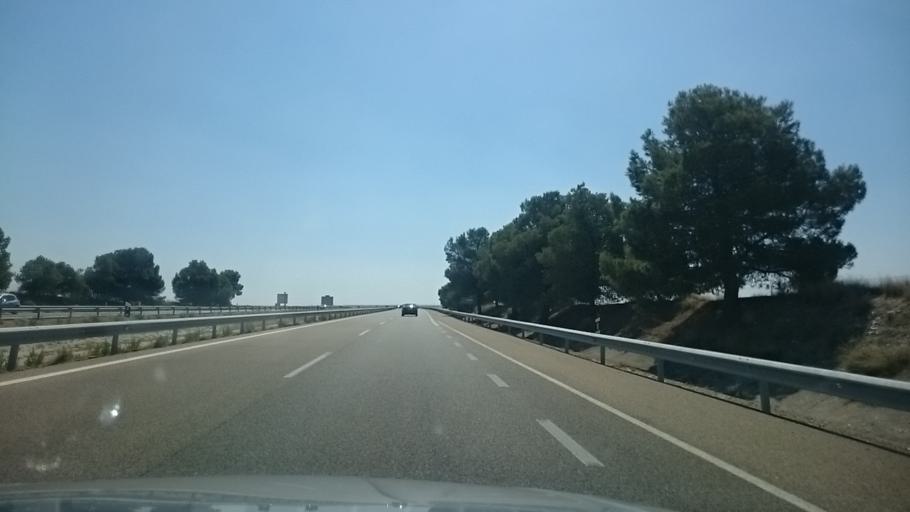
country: ES
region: Aragon
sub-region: Provincia de Zaragoza
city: Monegrillo
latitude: 41.5233
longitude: -0.3892
